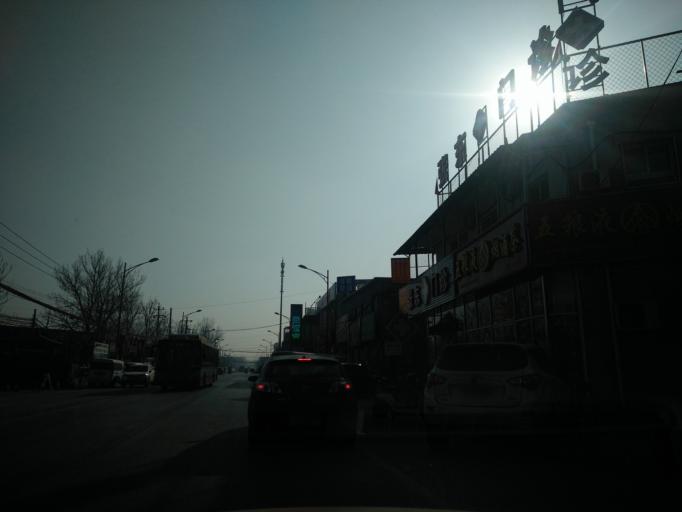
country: CN
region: Beijing
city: Jiugong
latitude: 39.8274
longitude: 116.4994
